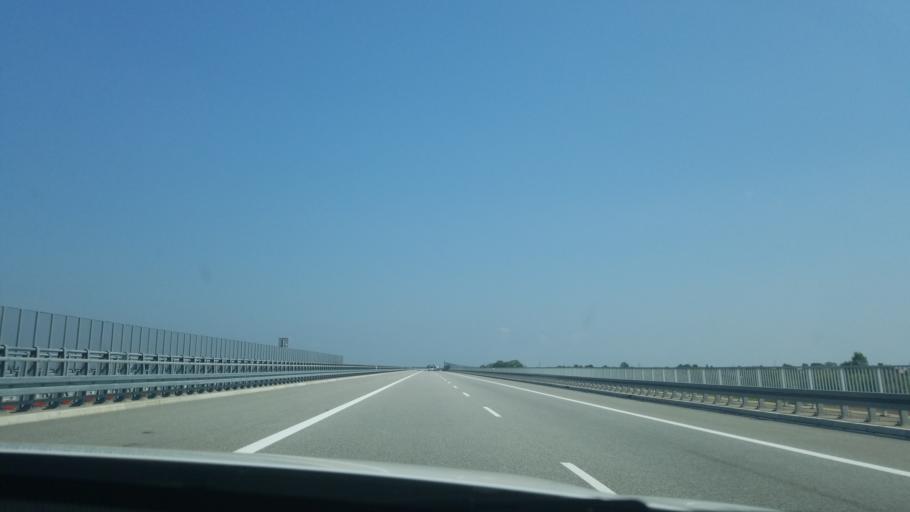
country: PL
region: Subcarpathian Voivodeship
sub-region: Powiat debicki
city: Zyrakow
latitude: 50.0840
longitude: 21.4183
